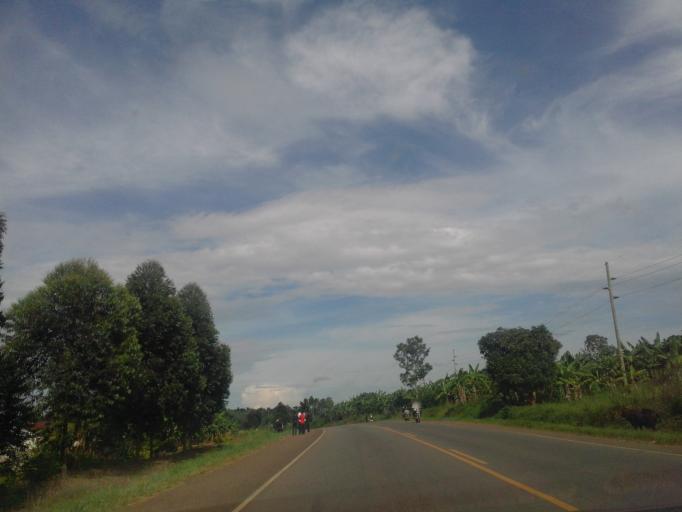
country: UG
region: Central Region
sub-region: Lwengo District
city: Lwengo
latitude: -0.3668
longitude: 31.5375
